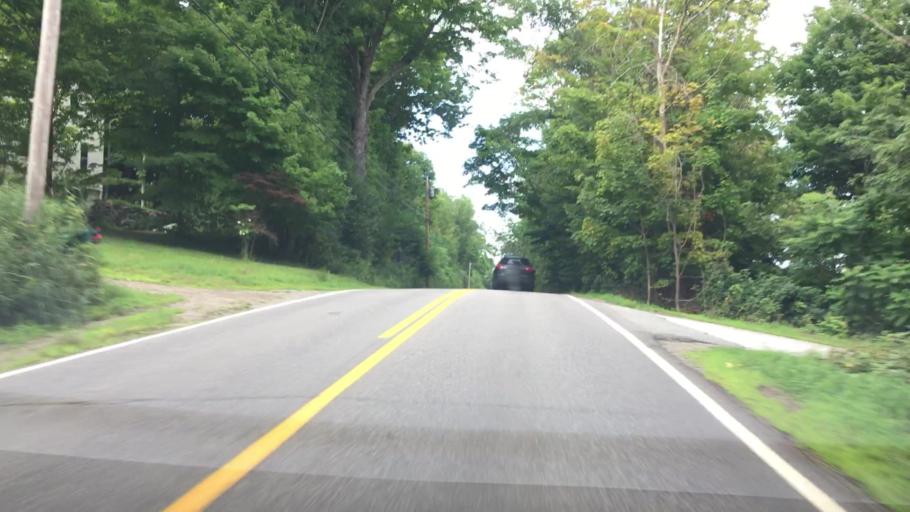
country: US
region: Maine
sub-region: Waldo County
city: Belfast
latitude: 44.3594
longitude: -69.0471
